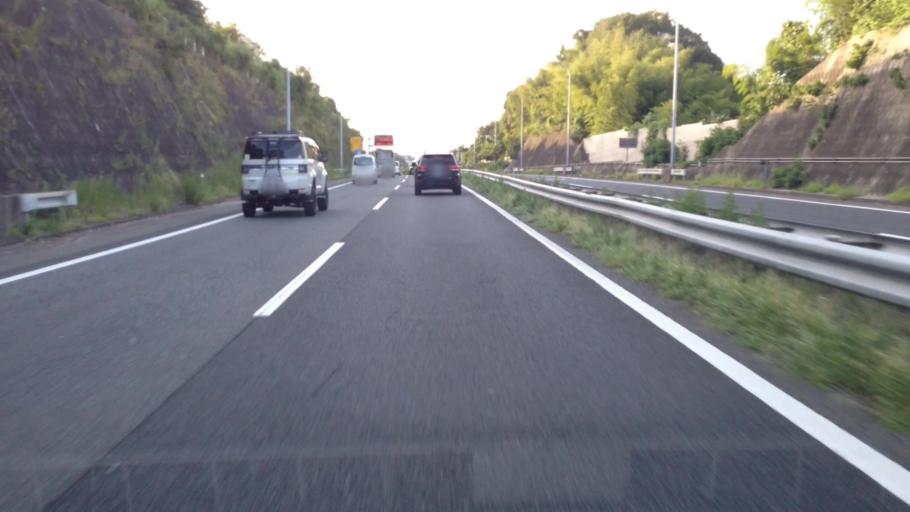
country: JP
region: Kanagawa
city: Kamakura
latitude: 35.3775
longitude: 139.5879
